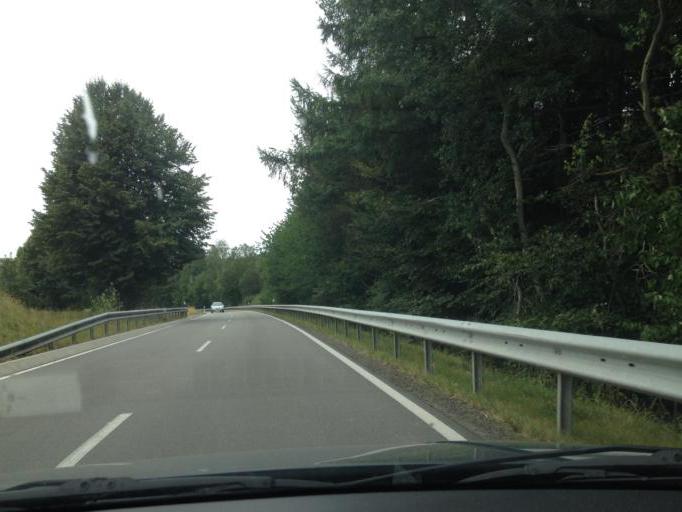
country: DE
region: Rheinland-Pfalz
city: Geiselberg
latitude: 49.3257
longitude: 7.6829
